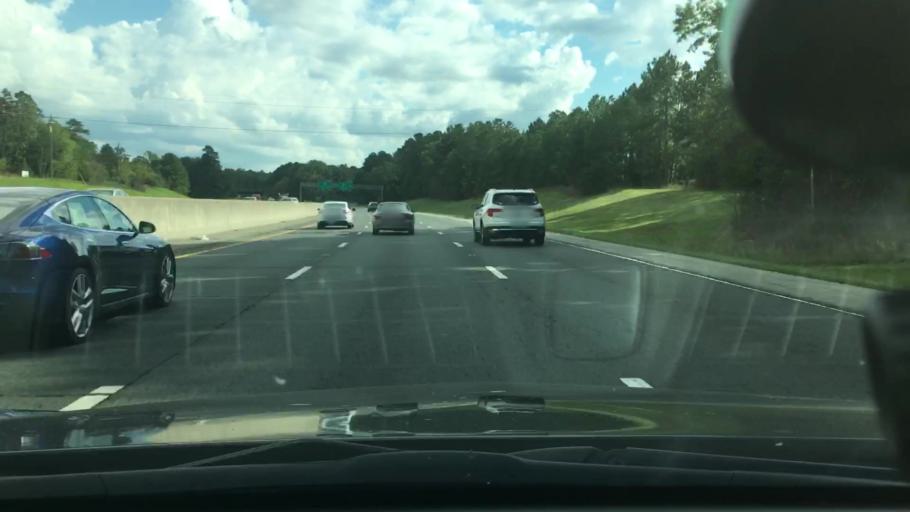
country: US
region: North Carolina
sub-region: Orange County
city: Chapel Hill
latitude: 35.9188
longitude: -78.9852
